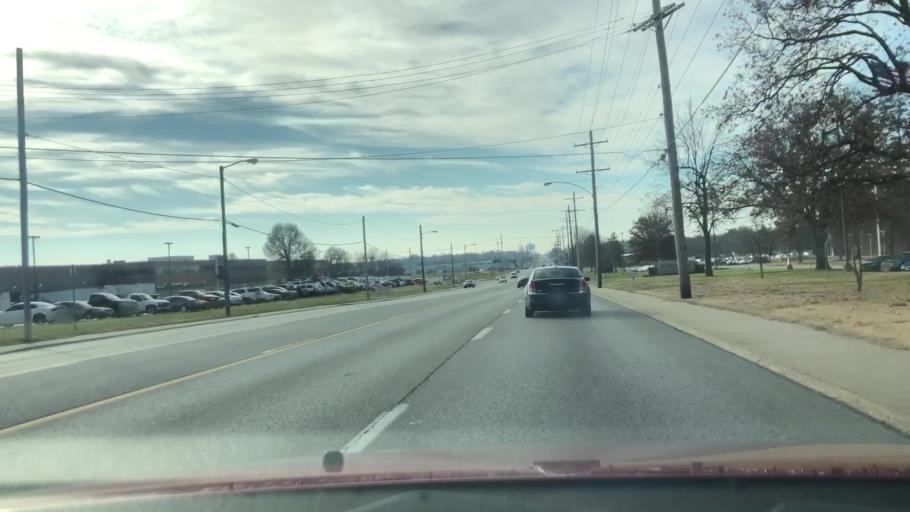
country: US
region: Missouri
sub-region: Greene County
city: Springfield
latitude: 37.2220
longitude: -93.2616
